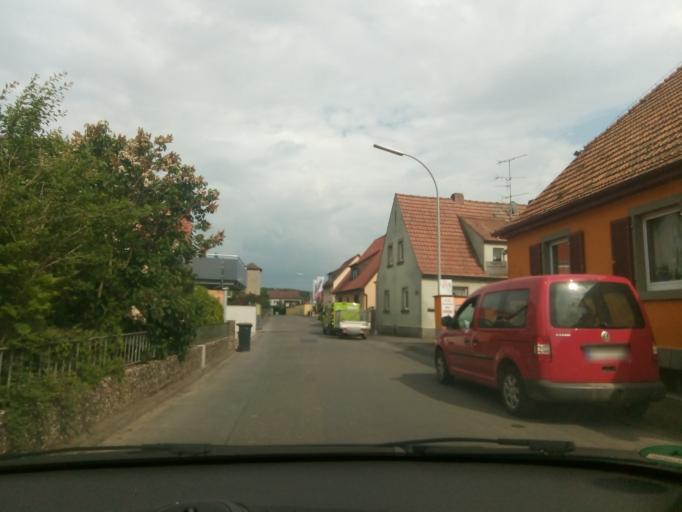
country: DE
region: Bavaria
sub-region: Regierungsbezirk Unterfranken
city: Volkach
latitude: 49.8649
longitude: 10.2350
